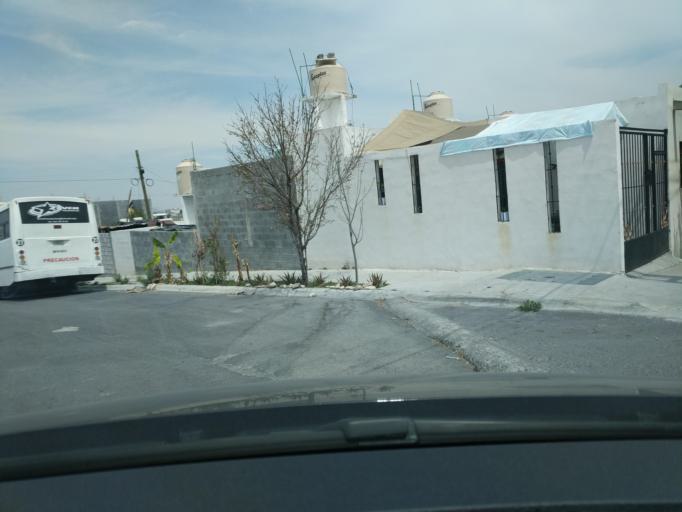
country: MX
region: Coahuila
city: Saltillo
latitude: 25.3450
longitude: -101.0058
